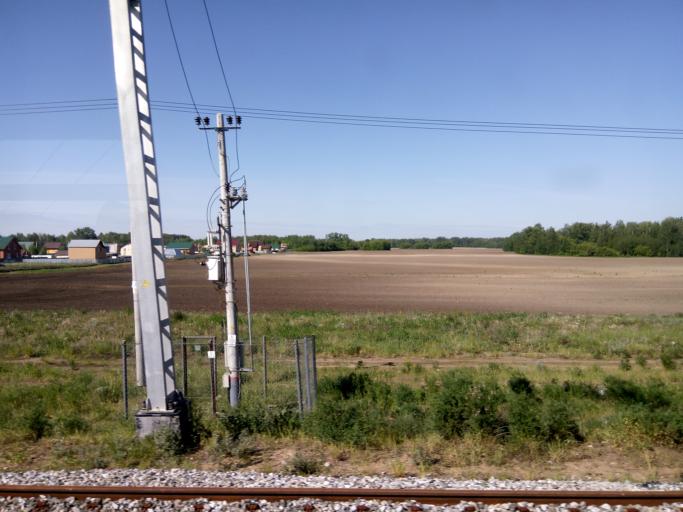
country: RU
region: Tatarstan
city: Stolbishchi
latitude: 55.6724
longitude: 49.2124
